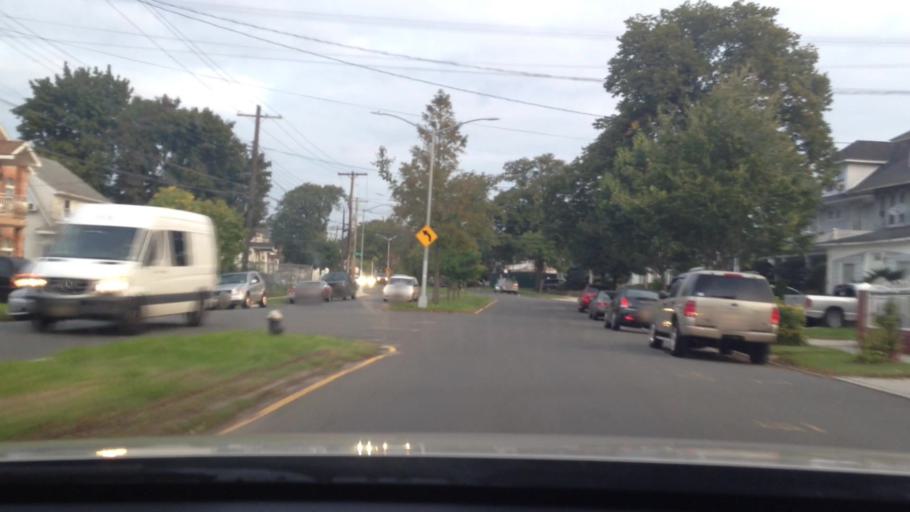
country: US
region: New York
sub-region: Nassau County
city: Bellerose Terrace
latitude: 40.7178
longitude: -73.7489
